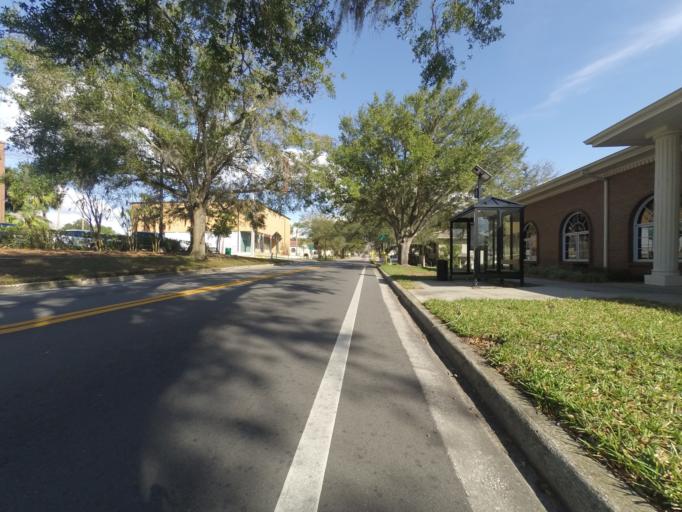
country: US
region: Florida
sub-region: Lake County
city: Mount Dora
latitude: 28.8005
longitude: -81.6431
